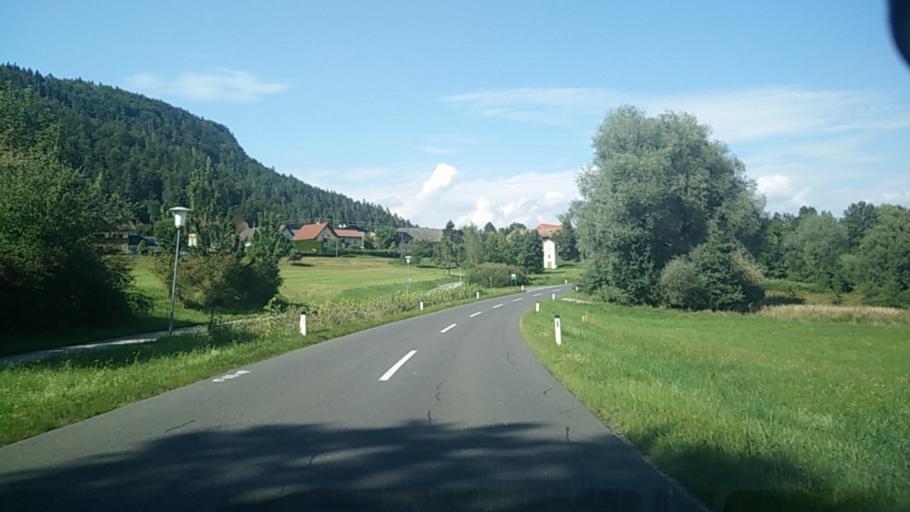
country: AT
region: Carinthia
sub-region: Politischer Bezirk Volkermarkt
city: Sittersdorf
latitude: 46.5898
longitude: 14.5645
